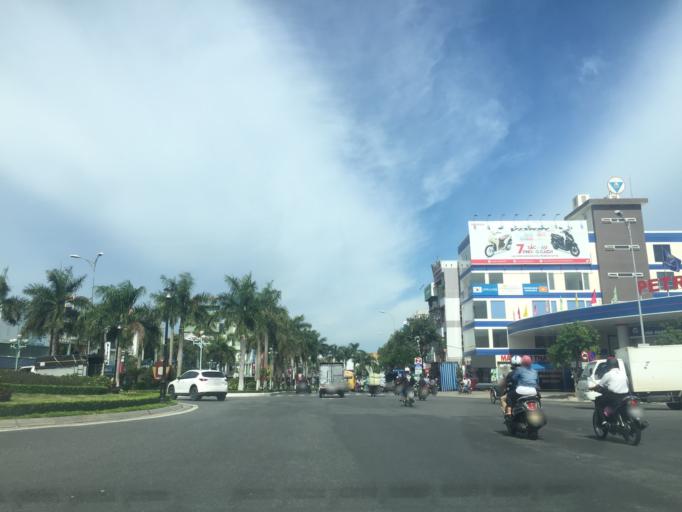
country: VN
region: Da Nang
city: Thanh Khe
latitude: 16.0650
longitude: 108.1833
